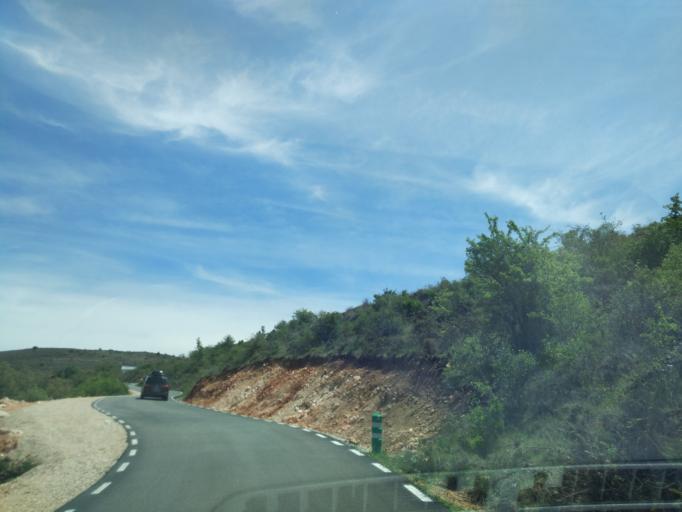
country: ES
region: Castille-La Mancha
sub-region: Provincia de Guadalajara
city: Torremocha del Campo
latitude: 41.0147
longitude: -2.6316
